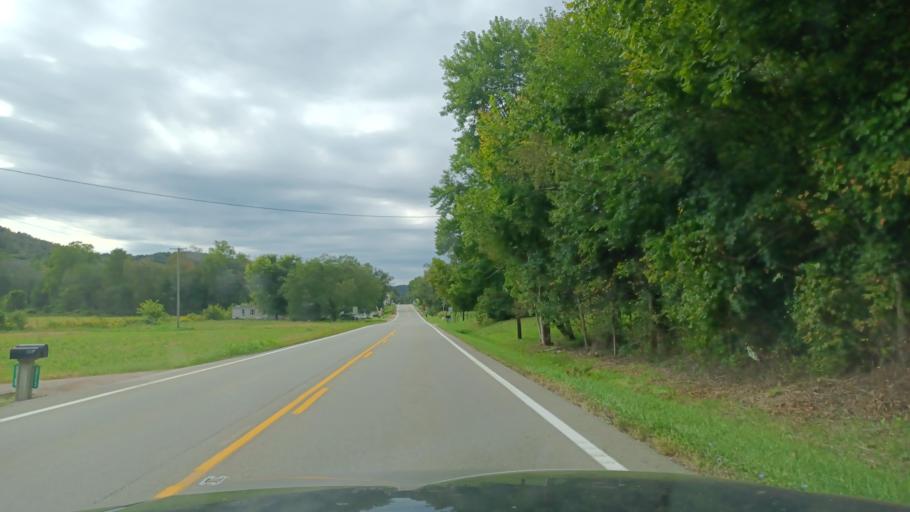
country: US
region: Ohio
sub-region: Vinton County
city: McArthur
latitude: 39.2724
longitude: -82.6013
